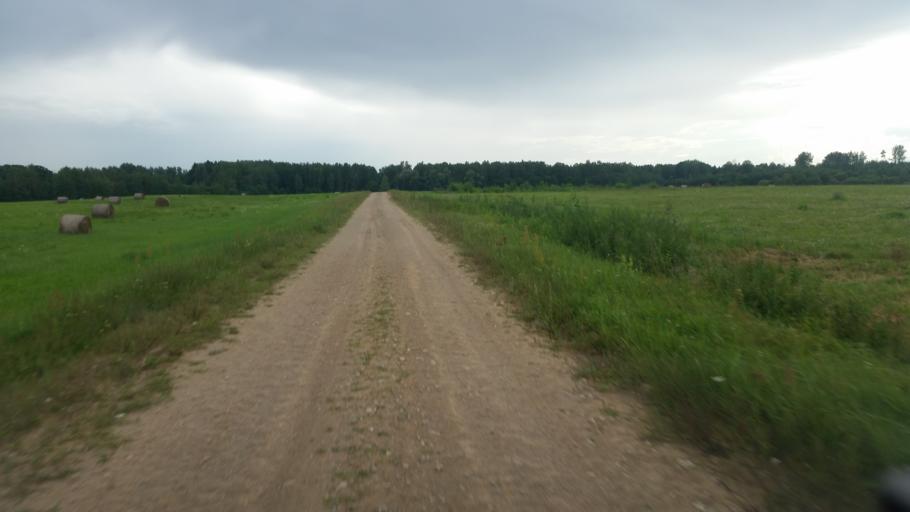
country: LV
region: Vecumnieki
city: Vecumnieki
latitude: 56.4464
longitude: 24.6374
